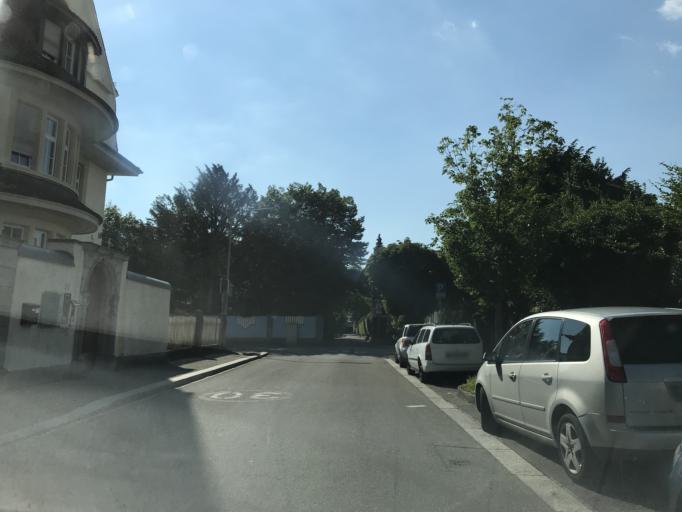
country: DE
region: Baden-Wuerttemberg
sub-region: Freiburg Region
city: Loerrach
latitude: 47.6172
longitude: 7.6636
